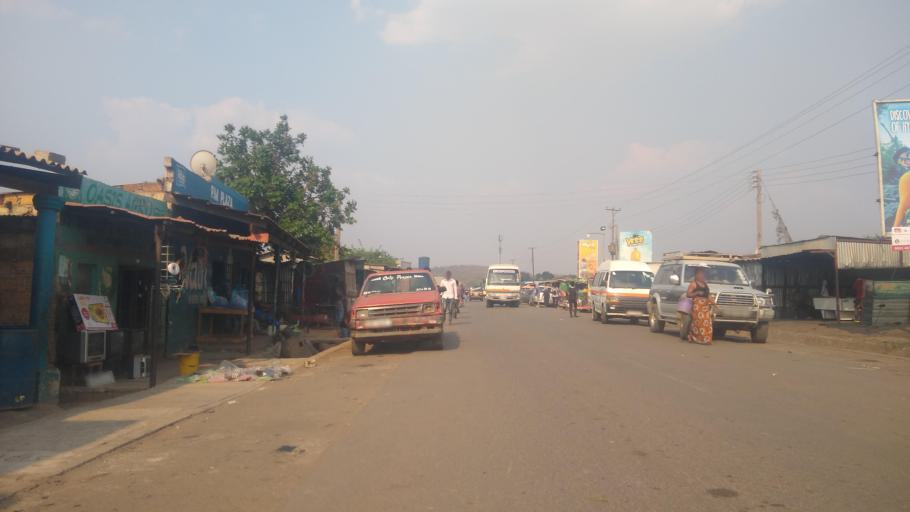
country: ZM
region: Lusaka
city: Lusaka
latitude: -15.4476
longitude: 28.3773
